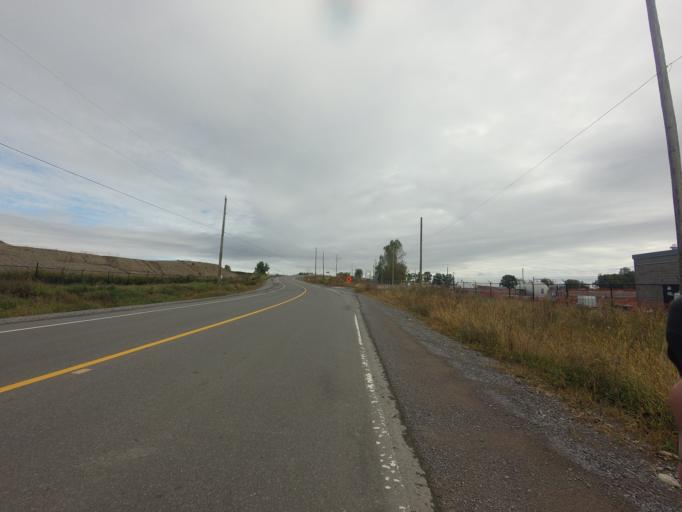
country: CA
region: Ontario
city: Cobourg
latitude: 43.9113
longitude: -78.4521
